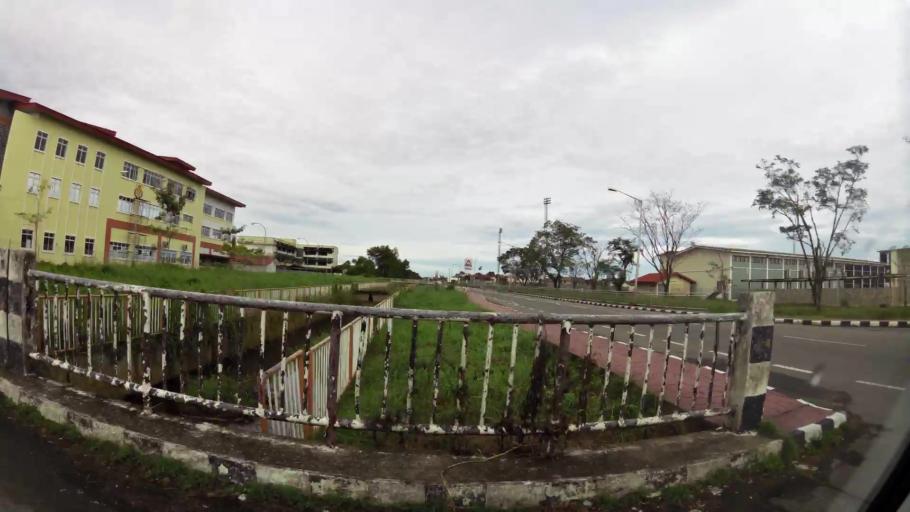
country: BN
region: Belait
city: Seria
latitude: 4.6083
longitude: 114.3322
